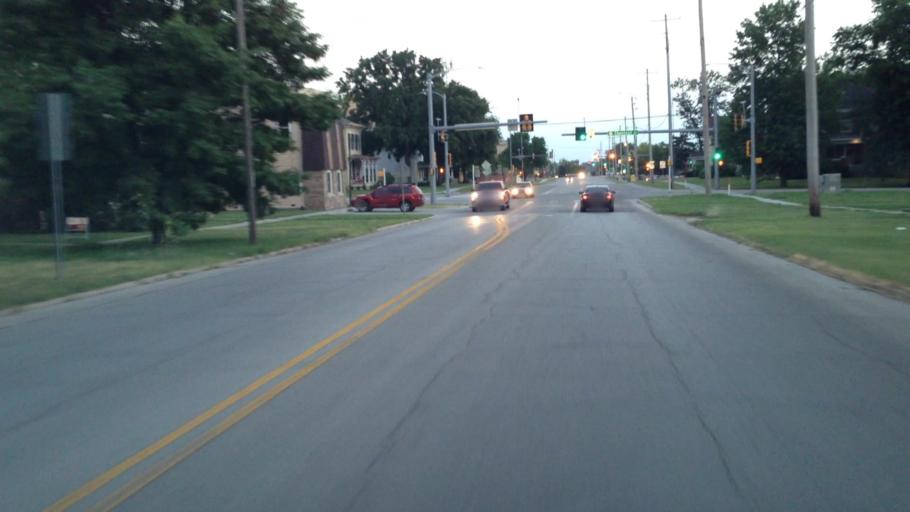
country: US
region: Kansas
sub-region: Montgomery County
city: Independence
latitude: 37.2274
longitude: -95.7108
